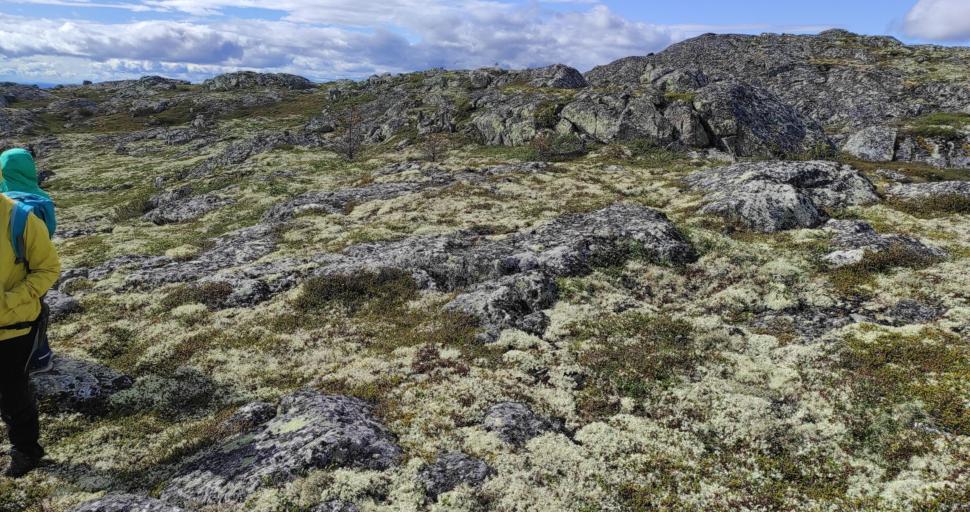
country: RU
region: Murmansk
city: Afrikanda
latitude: 67.0437
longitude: 32.9515
